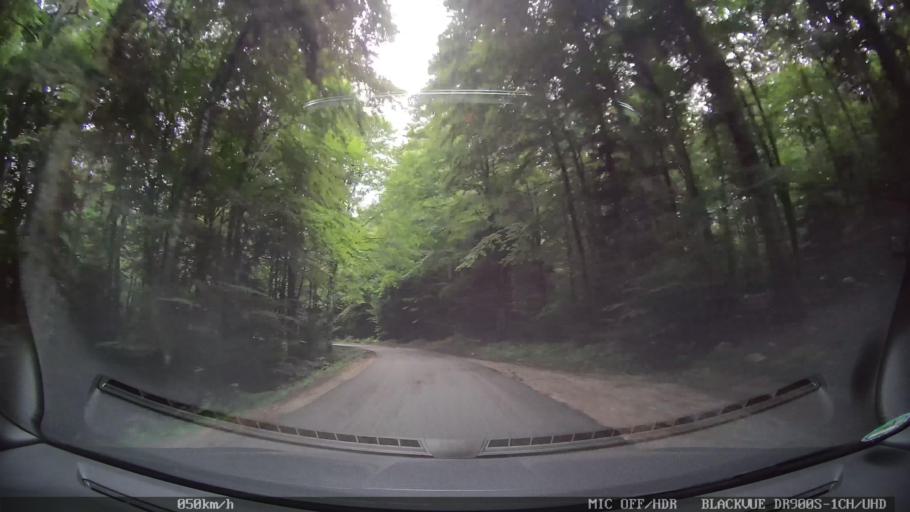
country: HR
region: Licko-Senjska
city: Jezerce
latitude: 44.9270
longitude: 15.5738
